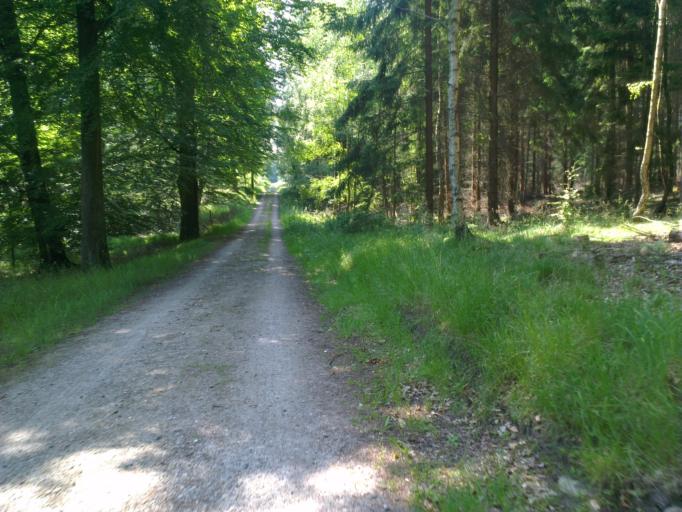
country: DK
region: Capital Region
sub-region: Allerod Kommune
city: Lillerod
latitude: 55.9152
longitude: 12.3589
